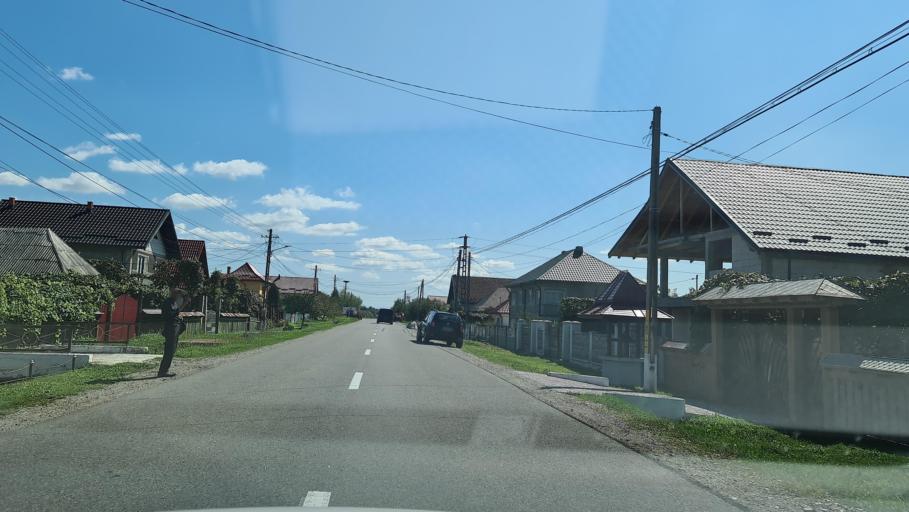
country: RO
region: Bacau
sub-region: Comuna Balcani
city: Balcani
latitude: 46.6429
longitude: 26.5698
